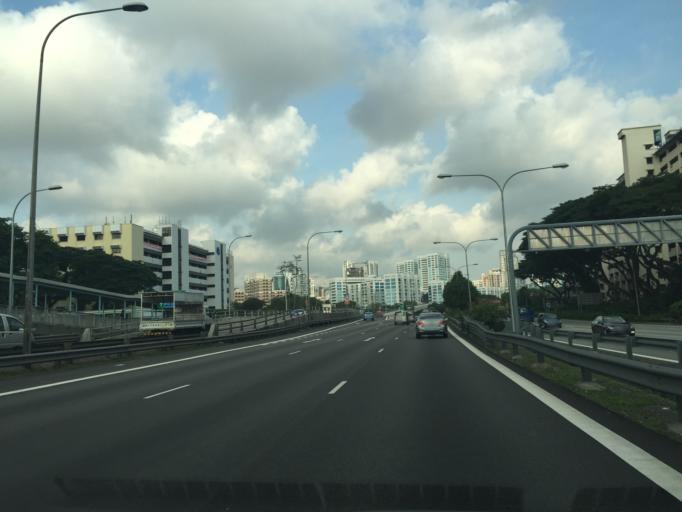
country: SG
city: Singapore
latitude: 1.3300
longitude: 103.8596
